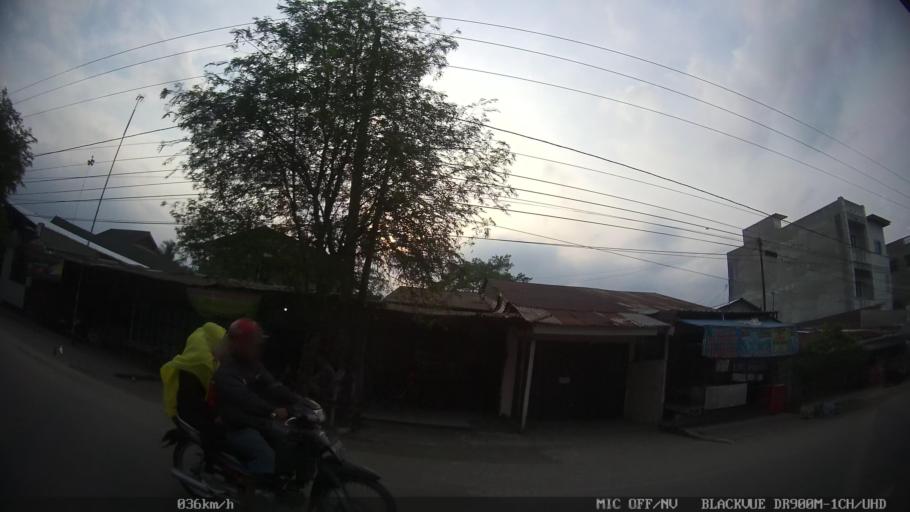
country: ID
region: North Sumatra
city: Sunggal
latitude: 3.5936
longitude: 98.6085
